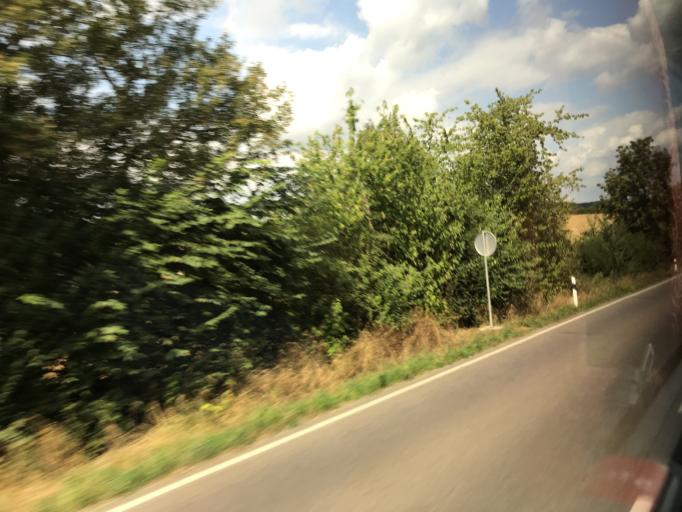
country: LU
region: Luxembourg
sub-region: Canton d'Esch-sur-Alzette
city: Frisange
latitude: 49.5245
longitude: 6.1844
